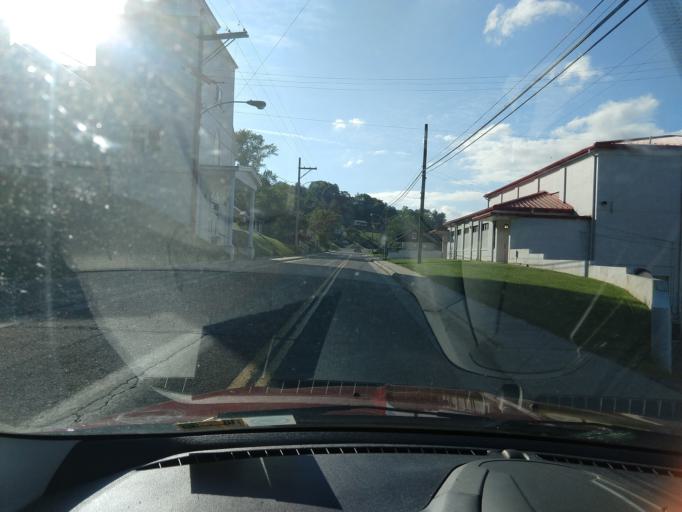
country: US
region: Virginia
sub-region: City of Galax
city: Galax
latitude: 36.7148
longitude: -80.9733
